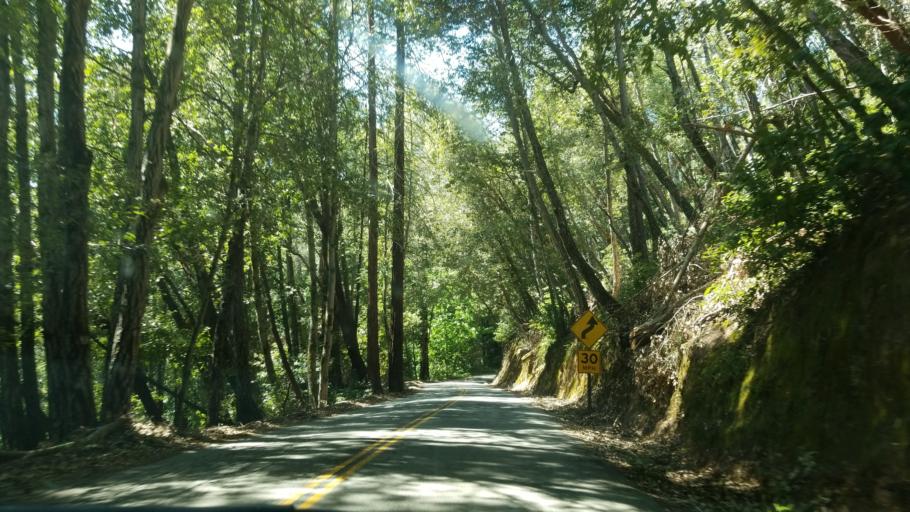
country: US
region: California
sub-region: Santa Cruz County
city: Day Valley
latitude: 37.0529
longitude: -121.8112
